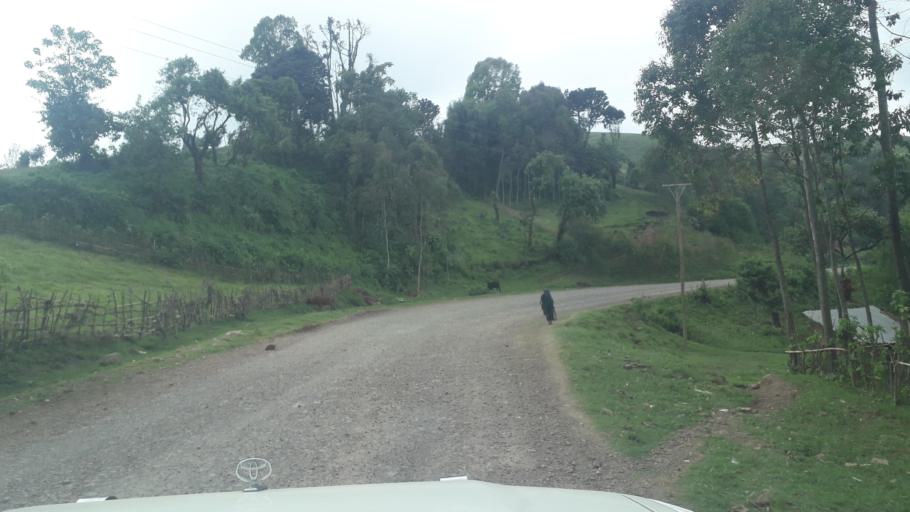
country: ET
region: Oromiya
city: Jima
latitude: 7.4473
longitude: 36.8791
